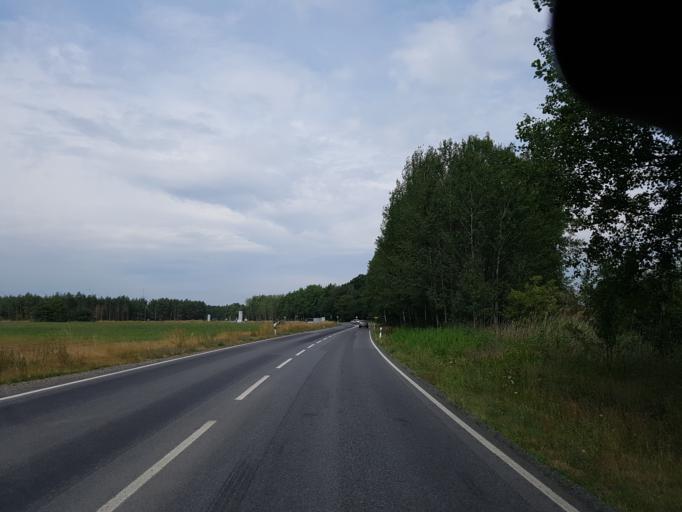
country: DE
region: Brandenburg
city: Schipkau
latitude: 51.5455
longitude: 13.9317
